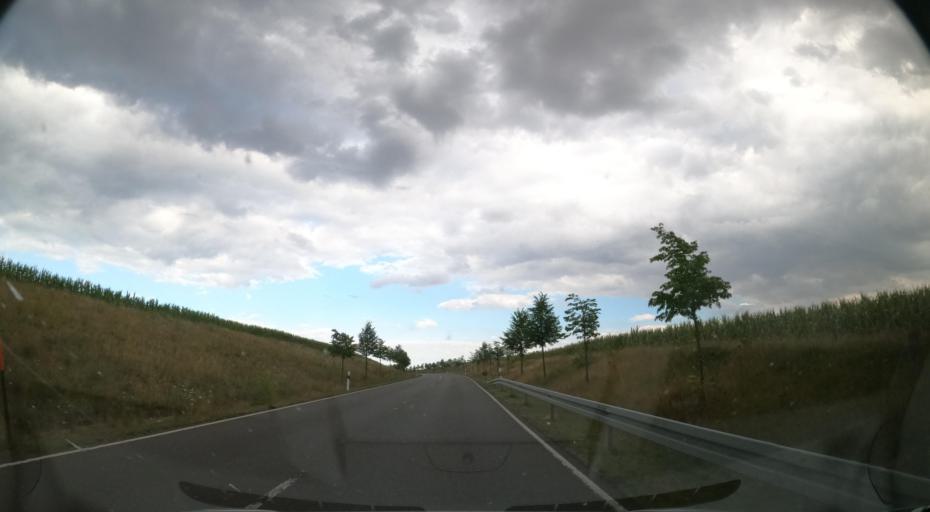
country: DE
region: Brandenburg
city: Goritz
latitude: 53.4862
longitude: 13.8534
